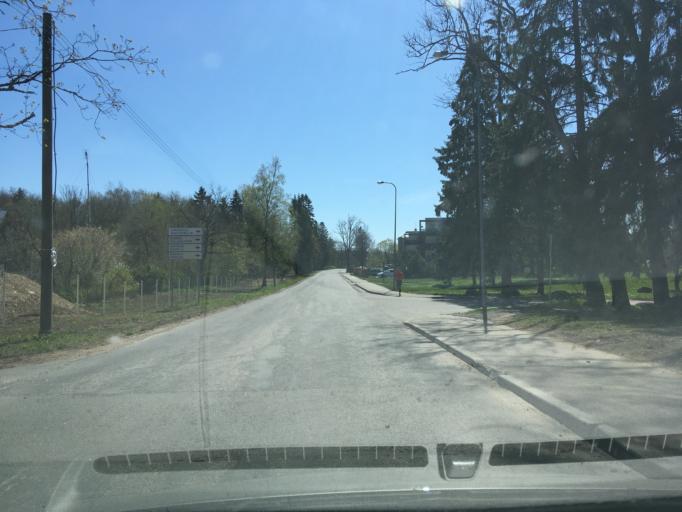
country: EE
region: Harju
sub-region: Raasiku vald
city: Arukula
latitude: 59.3662
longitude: 25.0817
